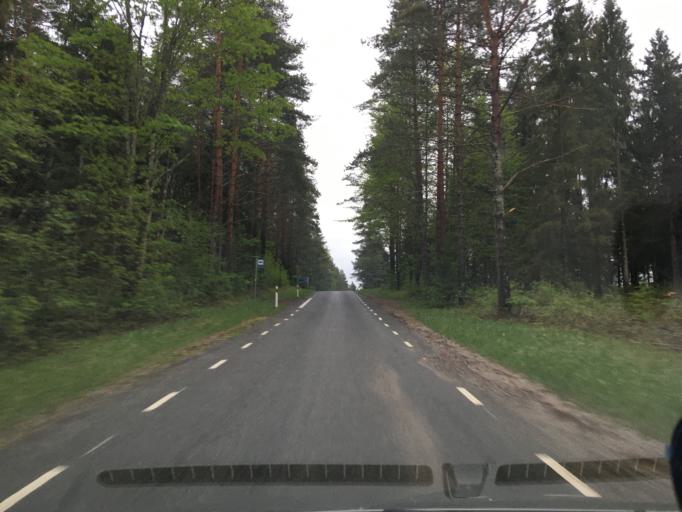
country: EE
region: Harju
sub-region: Keila linn
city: Keila
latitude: 59.1995
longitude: 24.4690
